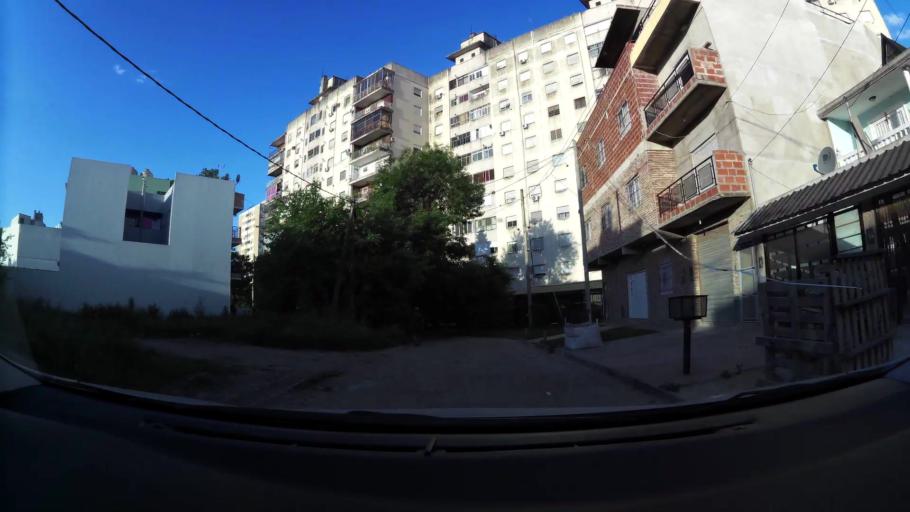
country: AR
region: Buenos Aires F.D.
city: Villa Lugano
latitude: -34.6958
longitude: -58.4782
